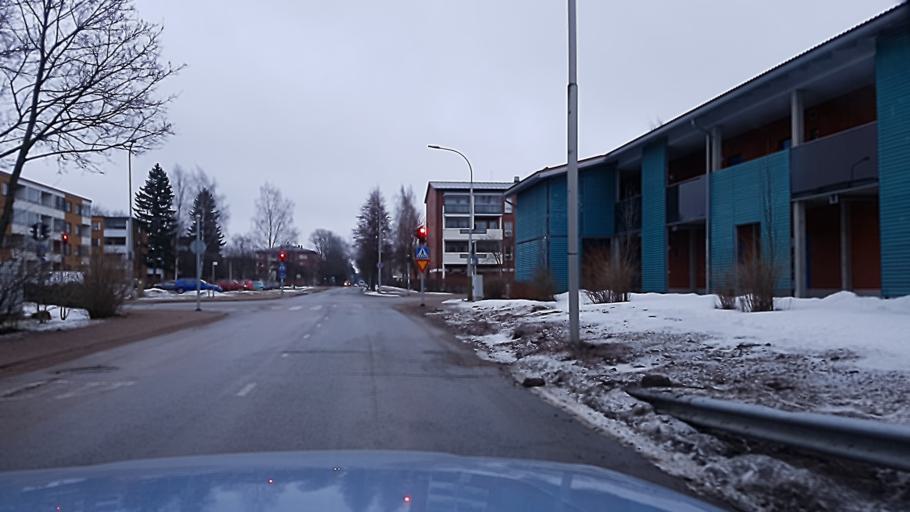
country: FI
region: Uusimaa
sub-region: Helsinki
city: Vantaa
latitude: 60.2940
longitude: 25.0152
